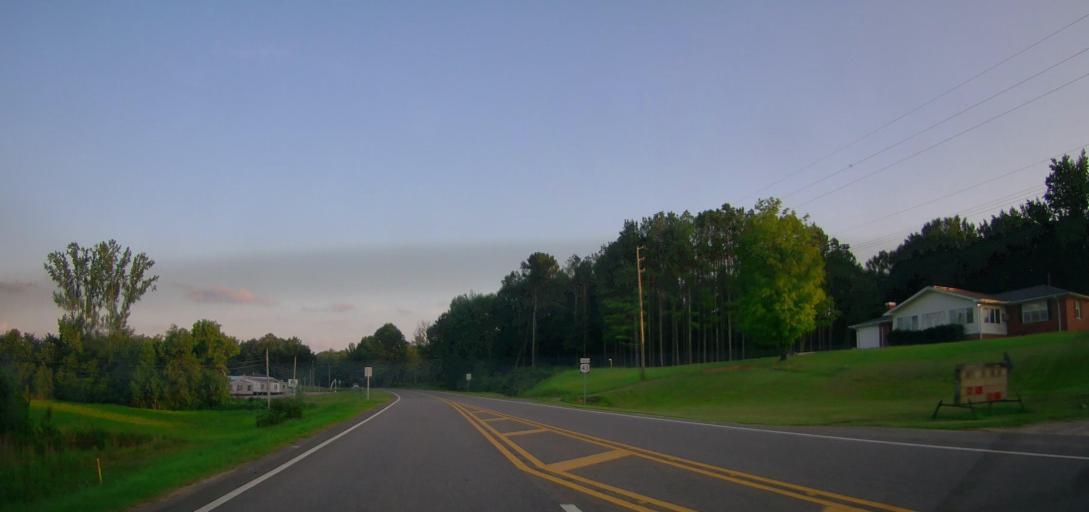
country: US
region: Alabama
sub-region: Marion County
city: Hamilton
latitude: 34.0984
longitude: -87.9884
